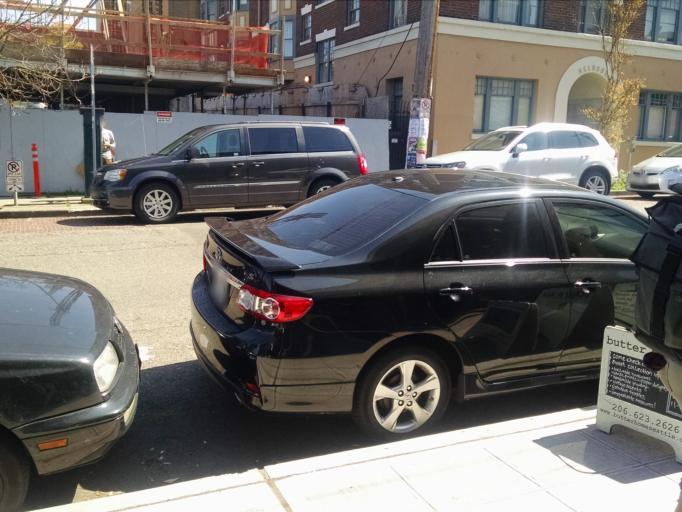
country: US
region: Washington
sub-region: King County
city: Seattle
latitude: 47.6147
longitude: -122.3280
